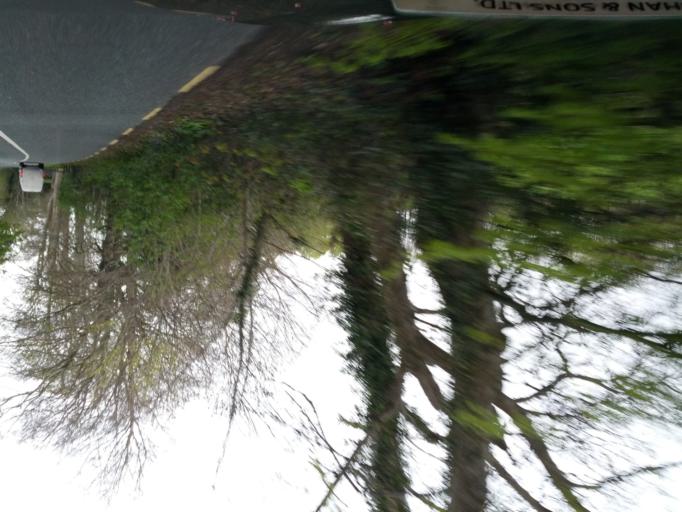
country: IE
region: Leinster
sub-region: An Mhi
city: Dunboyne
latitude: 53.3944
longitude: -6.4495
